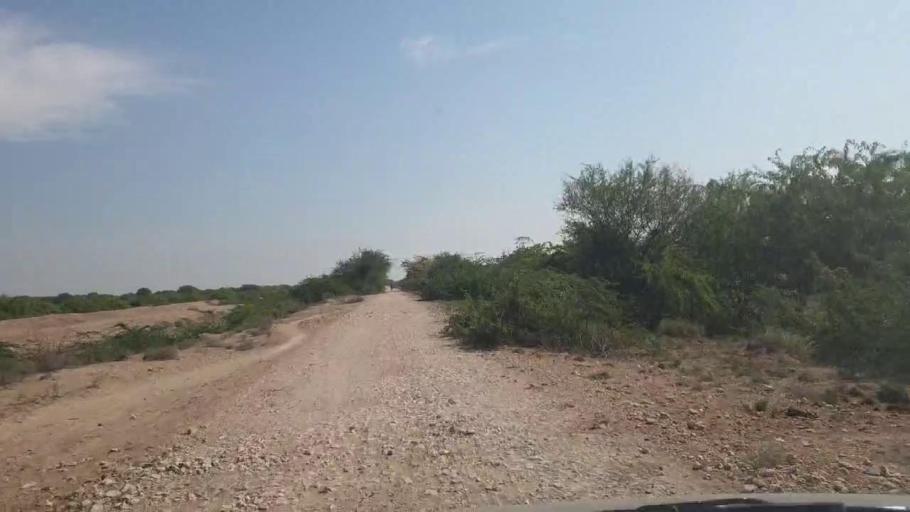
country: PK
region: Sindh
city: Digri
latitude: 24.9564
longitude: 69.1370
